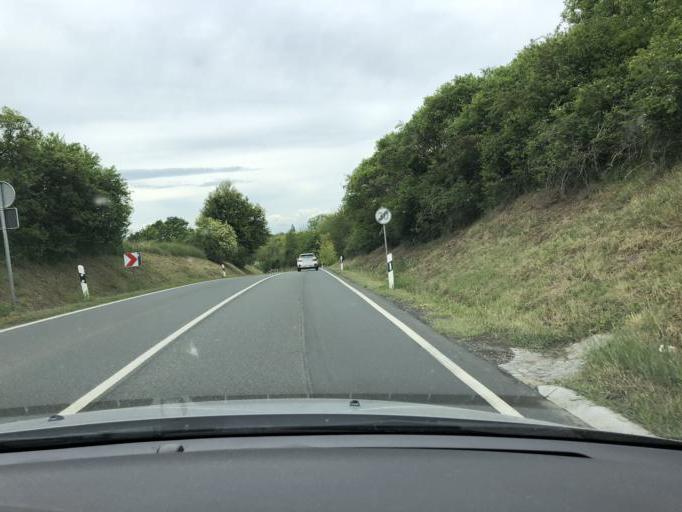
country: DE
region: Thuringia
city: Burgel
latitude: 50.9425
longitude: 11.7694
